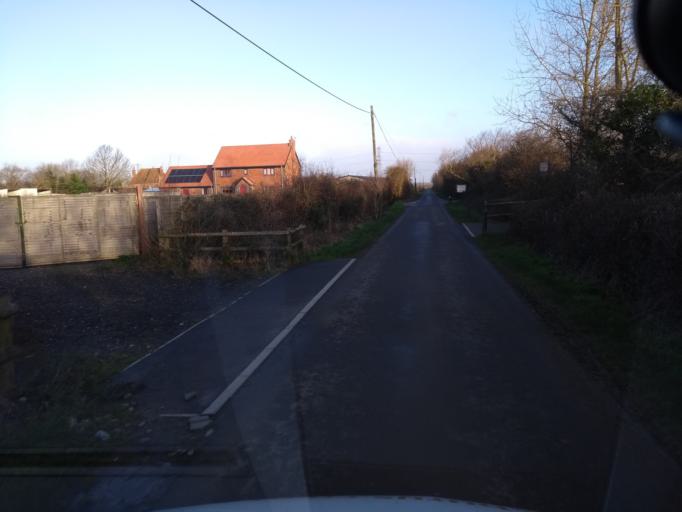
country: GB
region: England
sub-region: Somerset
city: Bridgwater
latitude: 51.1509
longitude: -3.0062
